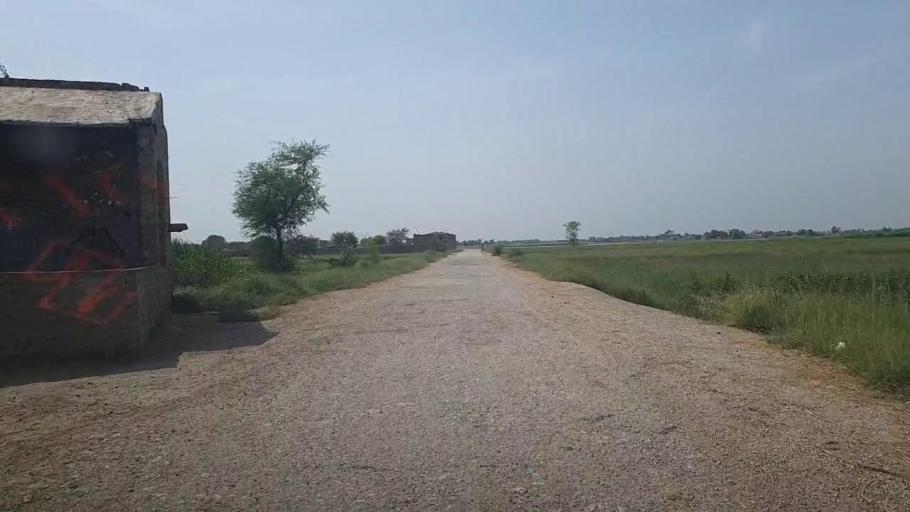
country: PK
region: Sindh
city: Ubauro
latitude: 28.1345
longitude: 69.8303
